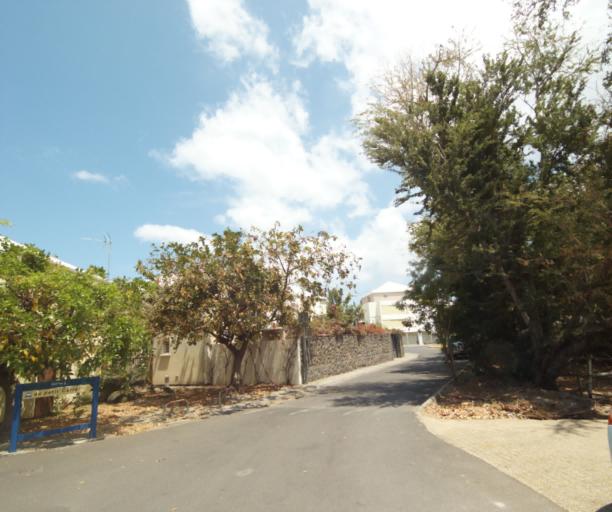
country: RE
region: Reunion
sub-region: Reunion
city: Saint-Paul
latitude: -21.0735
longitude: 55.2247
